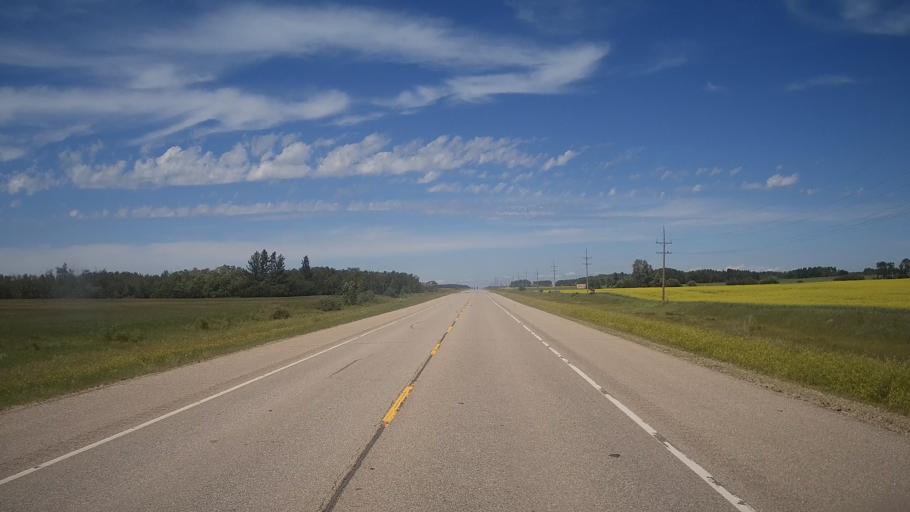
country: CA
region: Saskatchewan
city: Langenburg
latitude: 50.6567
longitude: -101.2761
